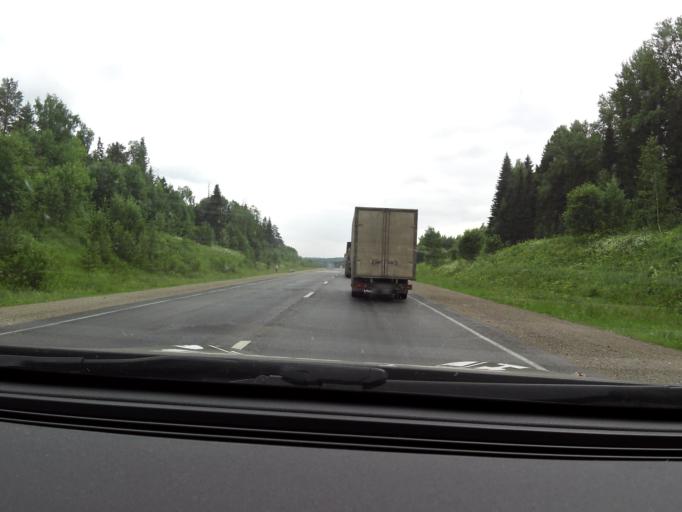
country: RU
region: Perm
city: Suksun
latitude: 57.1345
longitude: 57.2983
